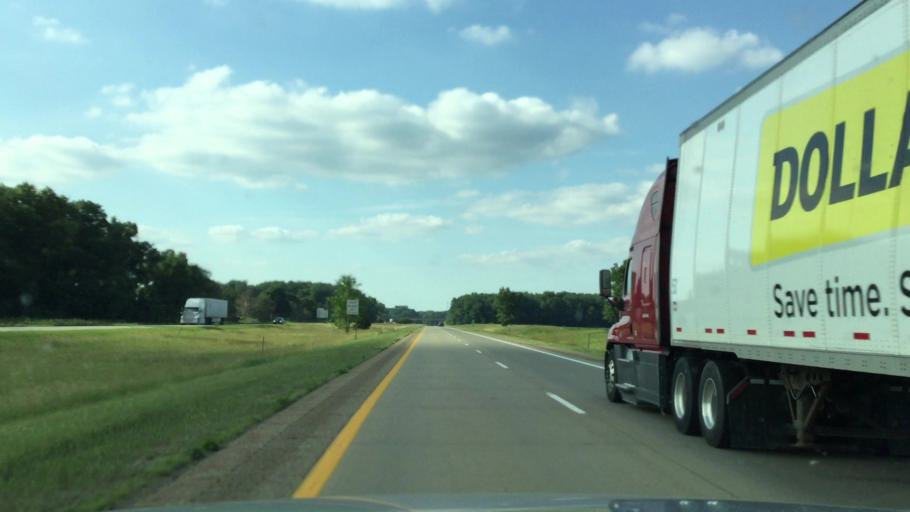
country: US
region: Michigan
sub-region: Branch County
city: Union City
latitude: 42.1220
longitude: -84.9953
